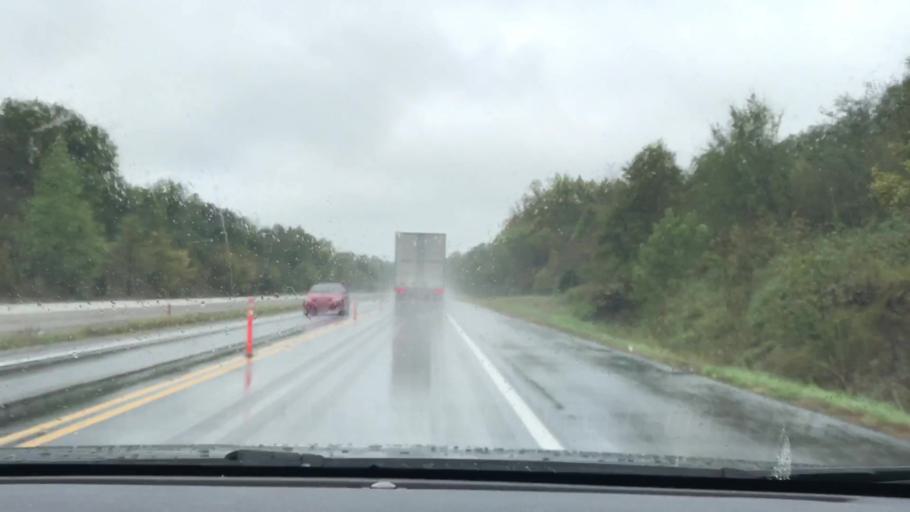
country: US
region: Kentucky
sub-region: Christian County
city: Hopkinsville
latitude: 37.0072
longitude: -87.4600
